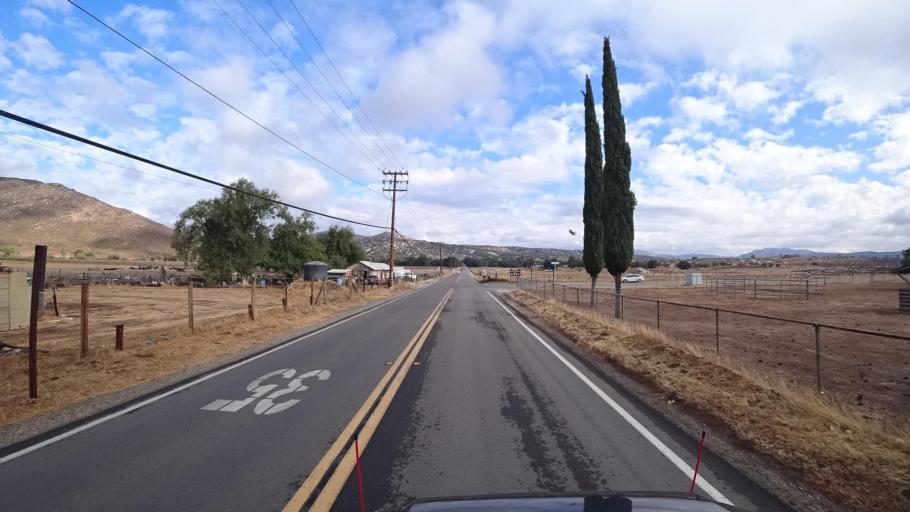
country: MX
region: Baja California
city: Tecate
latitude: 32.6146
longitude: -116.6133
